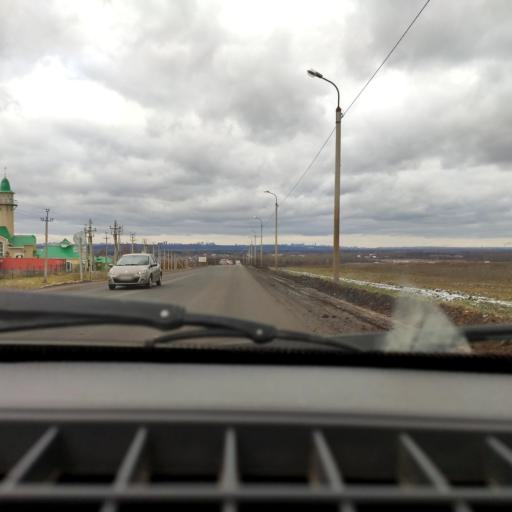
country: RU
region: Bashkortostan
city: Kabakovo
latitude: 54.6343
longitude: 56.0953
